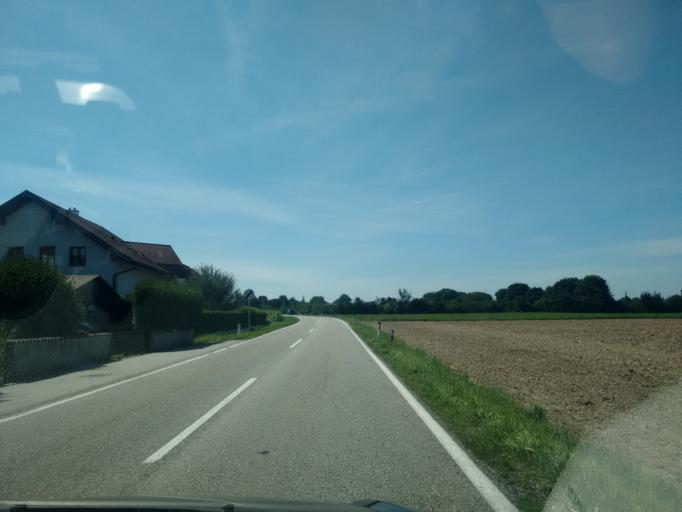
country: DE
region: Bavaria
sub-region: Lower Bavaria
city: Simbach am Inn
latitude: 48.2390
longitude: 13.0198
